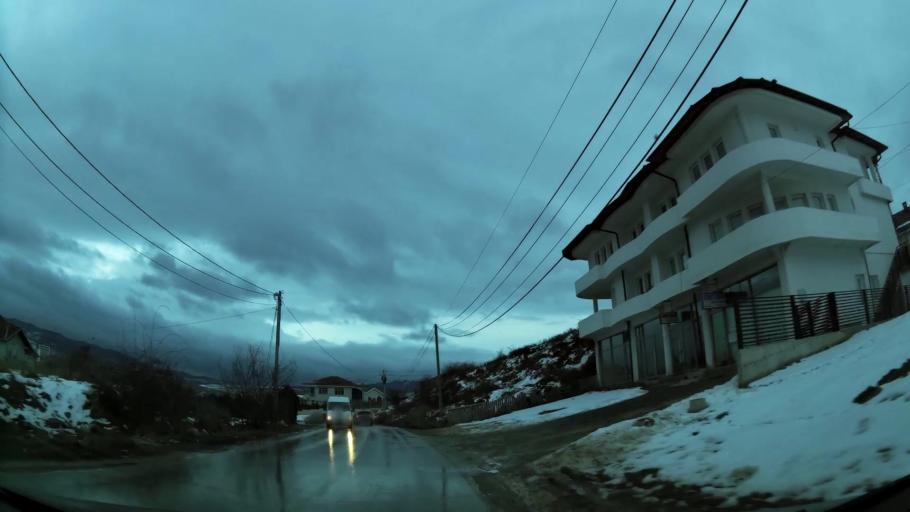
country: XK
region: Pristina
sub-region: Komuna e Prishtines
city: Pristina
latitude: 42.6292
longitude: 21.1647
